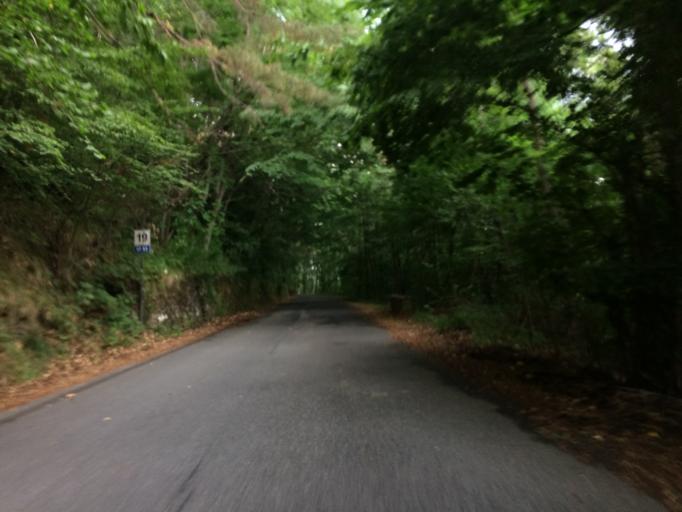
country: IT
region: Liguria
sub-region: Provincia di Imperia
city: Triora
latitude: 43.9845
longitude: 7.7613
